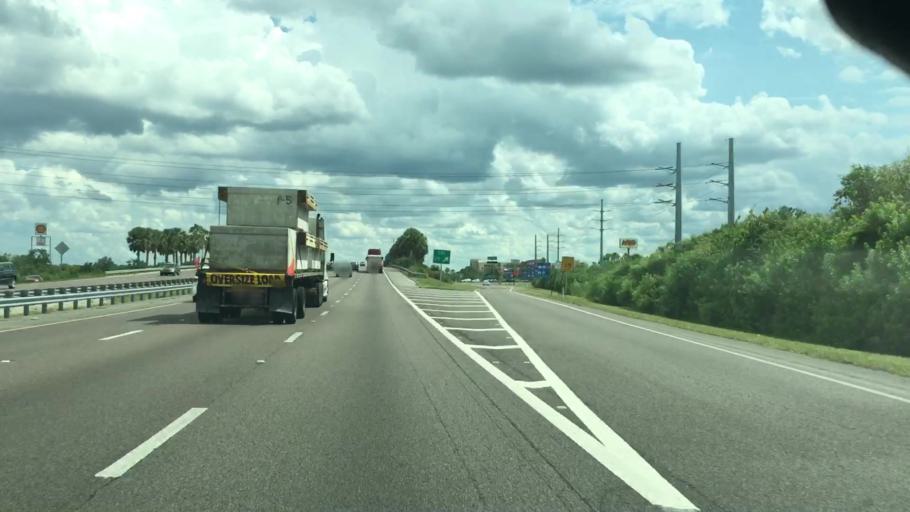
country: US
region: Florida
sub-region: Brevard County
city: Titusville
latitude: 28.5552
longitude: -80.8517
